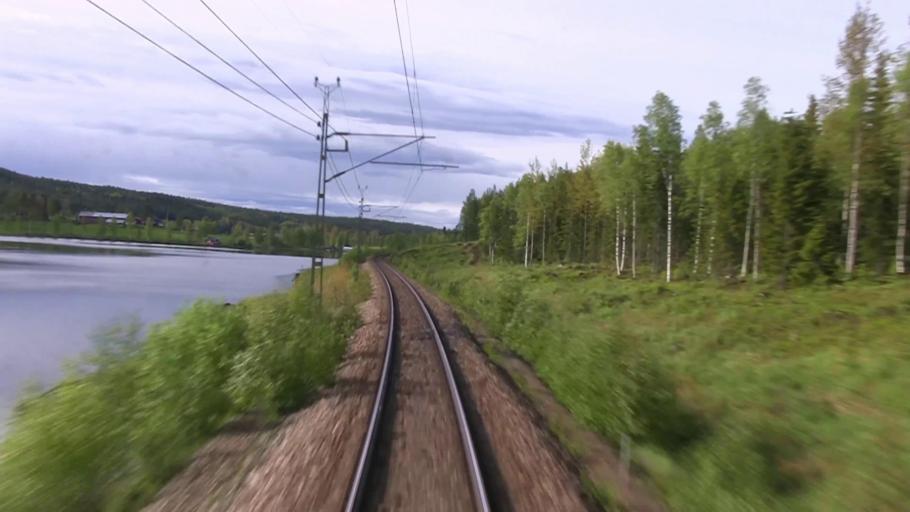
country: SE
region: Vaesterbotten
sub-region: Vindelns Kommun
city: Vindeln
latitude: 64.1140
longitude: 19.6909
